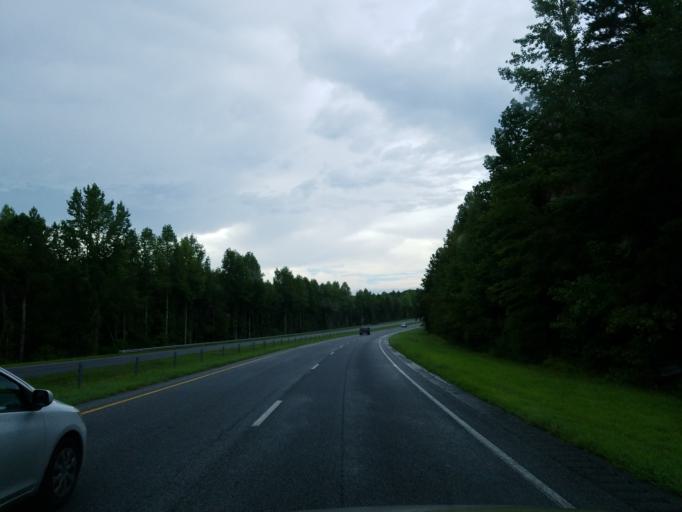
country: US
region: Georgia
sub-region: Lumpkin County
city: Dahlonega
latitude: 34.4367
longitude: -83.9938
